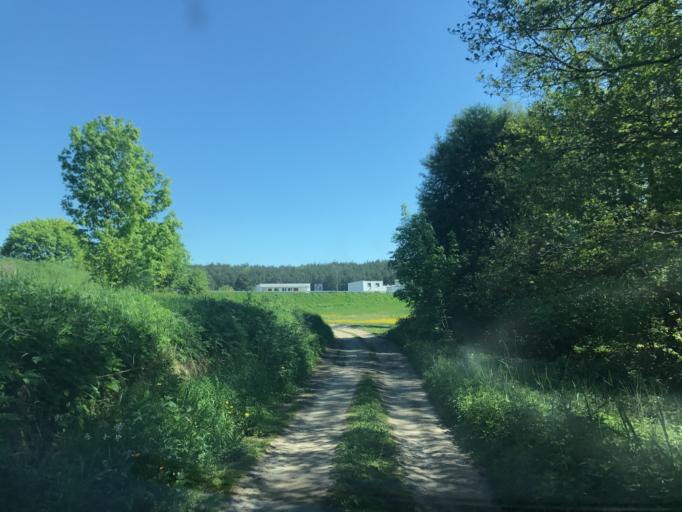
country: PL
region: Warmian-Masurian Voivodeship
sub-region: Powiat dzialdowski
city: Lidzbark
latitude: 53.2681
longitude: 19.8140
